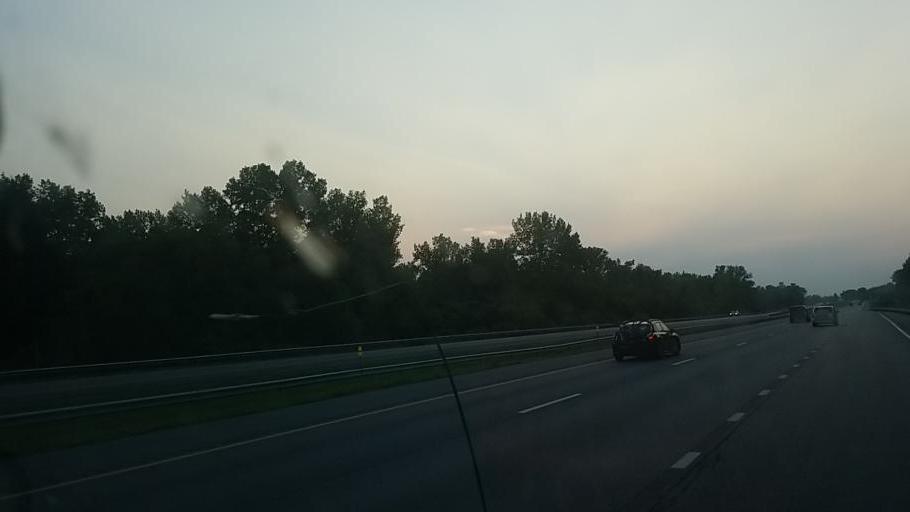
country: US
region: New York
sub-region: Herkimer County
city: Frankfort
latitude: 43.0777
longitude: -75.1066
